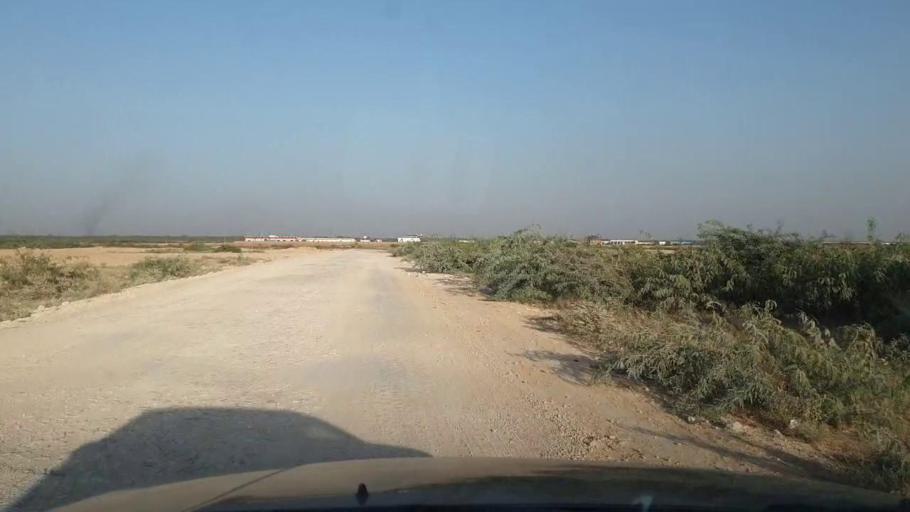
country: PK
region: Sindh
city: Kotri
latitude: 25.2163
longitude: 68.2311
